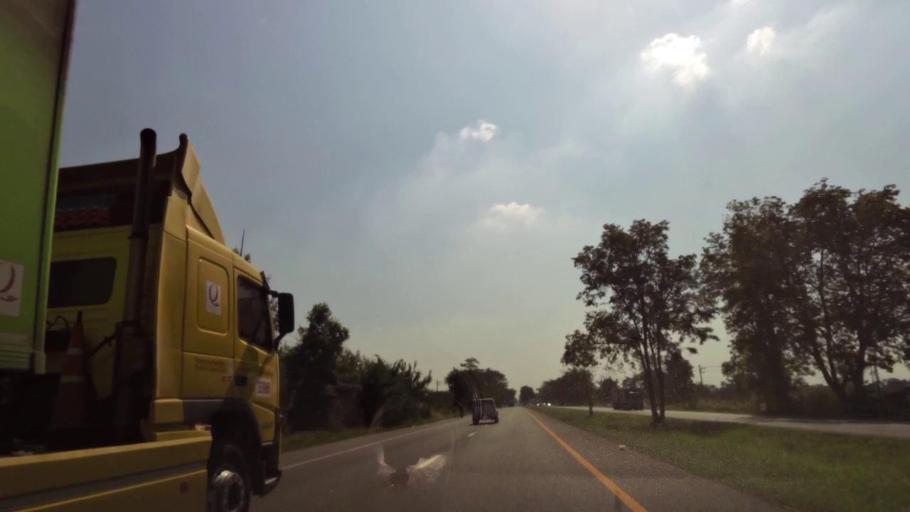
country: TH
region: Phichit
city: Bueng Na Rang
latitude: 16.2270
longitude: 100.1261
